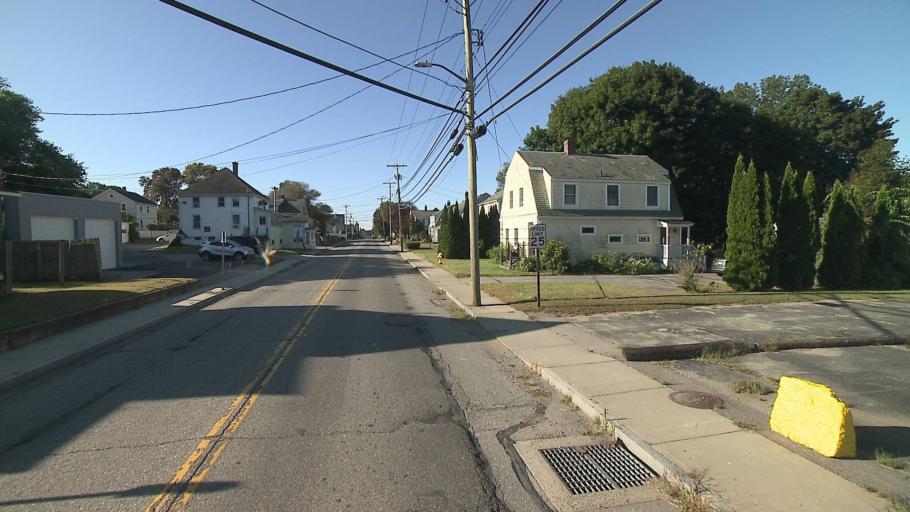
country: US
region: Connecticut
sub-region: New London County
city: Jewett City
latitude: 41.6130
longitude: -71.9796
